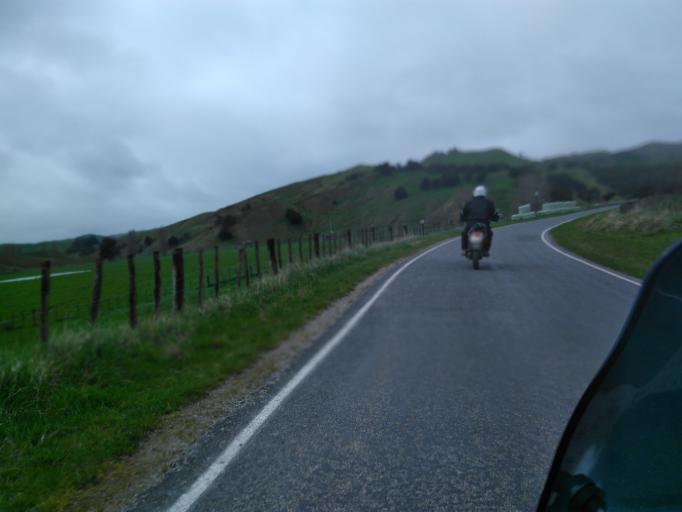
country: NZ
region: Gisborne
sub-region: Gisborne District
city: Gisborne
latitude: -38.6348
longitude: 177.6934
